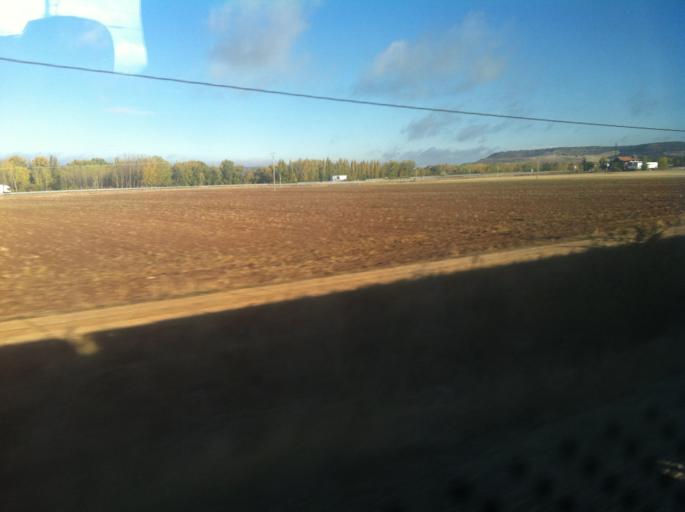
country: ES
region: Castille and Leon
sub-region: Provincia de Palencia
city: Cordovilla la Real
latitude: 42.0424
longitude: -4.2575
